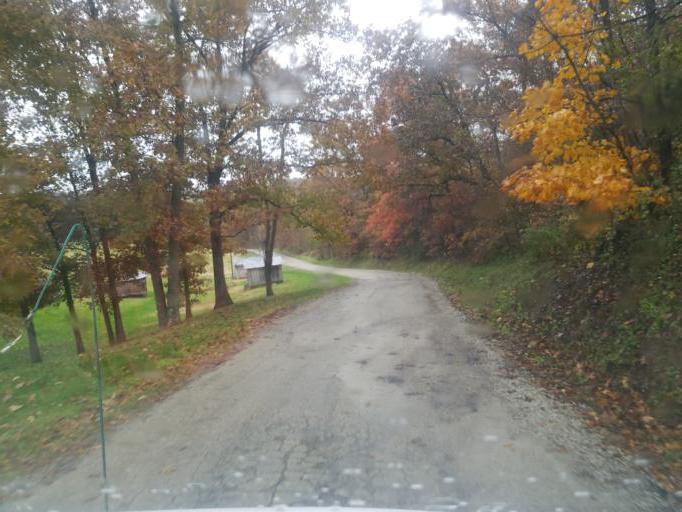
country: US
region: Ohio
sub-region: Washington County
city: Beverly
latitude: 39.4670
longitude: -81.6601
